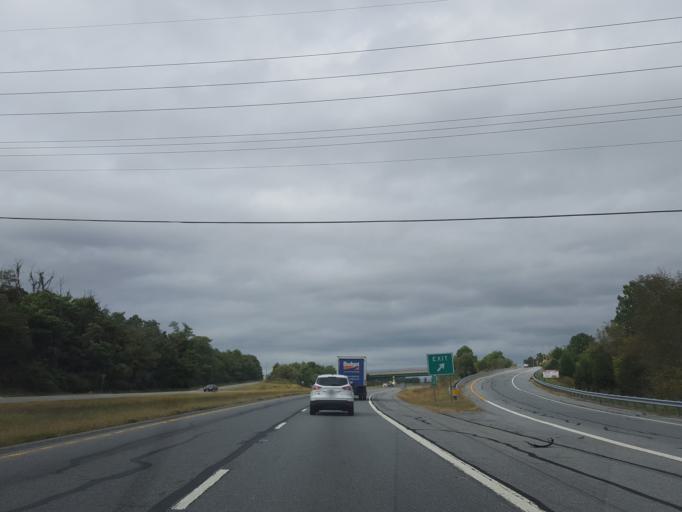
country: US
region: Maryland
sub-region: Frederick County
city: Jefferson
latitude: 39.3549
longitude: -77.5784
